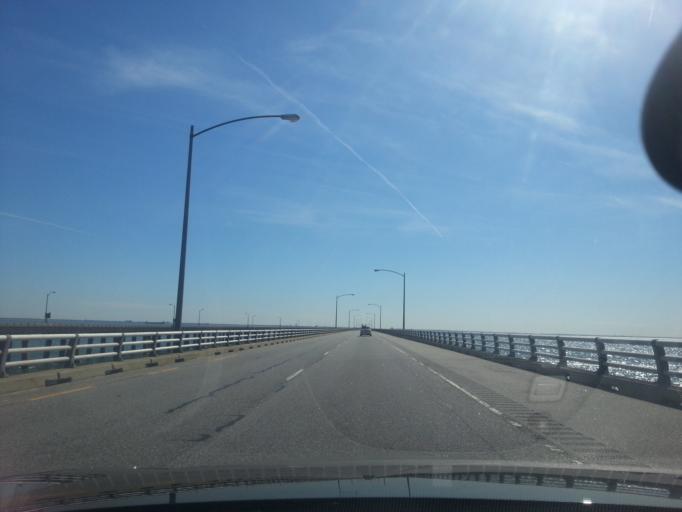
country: US
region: Virginia
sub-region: City of Virginia Beach
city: Virginia Beach
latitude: 37.0220
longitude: -76.0905
